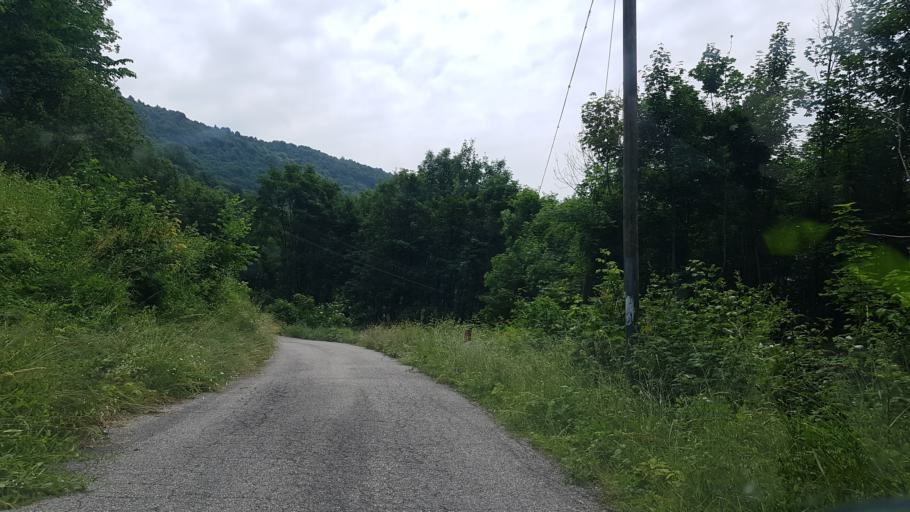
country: IT
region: Friuli Venezia Giulia
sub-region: Provincia di Udine
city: Torreano
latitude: 46.1758
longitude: 13.4329
